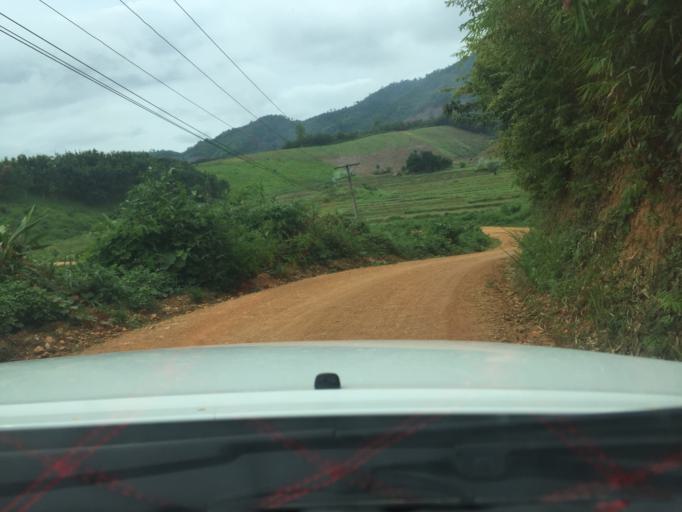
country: TH
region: Phayao
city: Phu Sang
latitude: 19.7687
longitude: 100.5523
